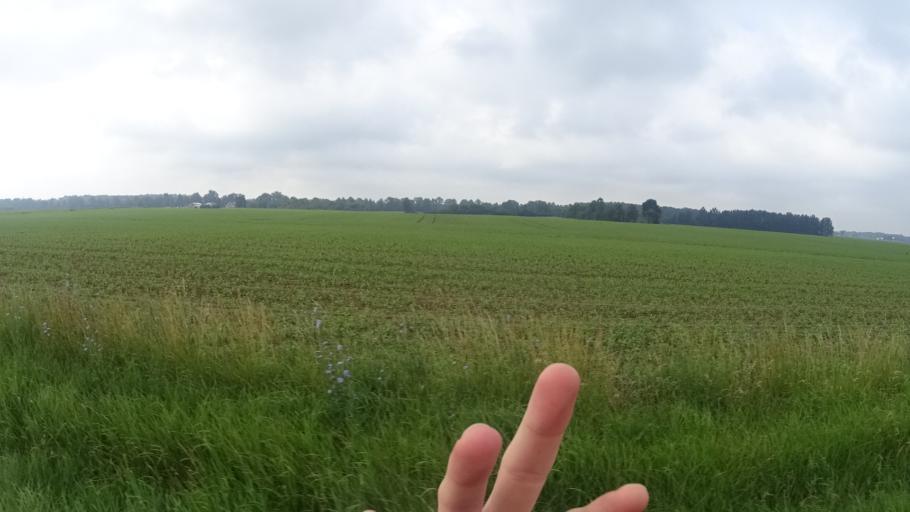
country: US
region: Ohio
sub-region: Huron County
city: Wakeman
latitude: 41.2798
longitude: -82.4946
